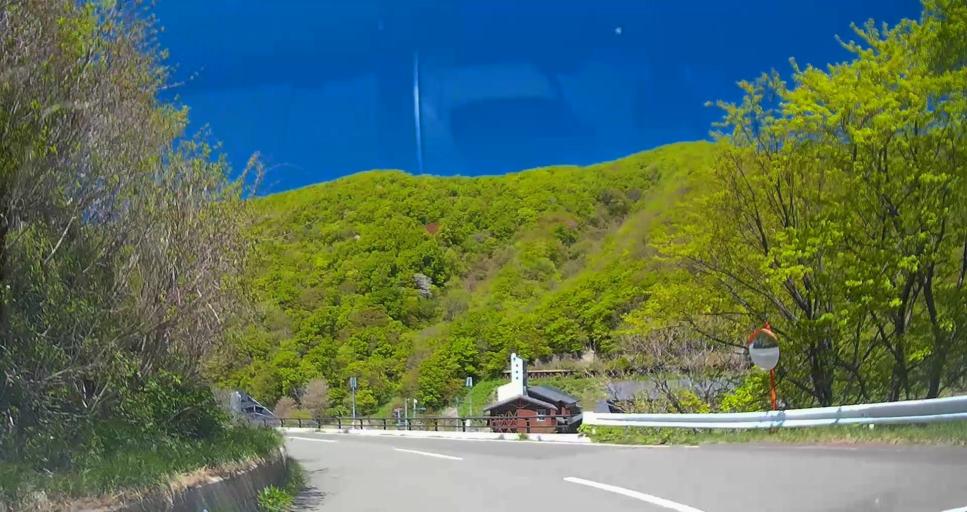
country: JP
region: Aomori
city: Mutsu
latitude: 41.3264
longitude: 140.8139
